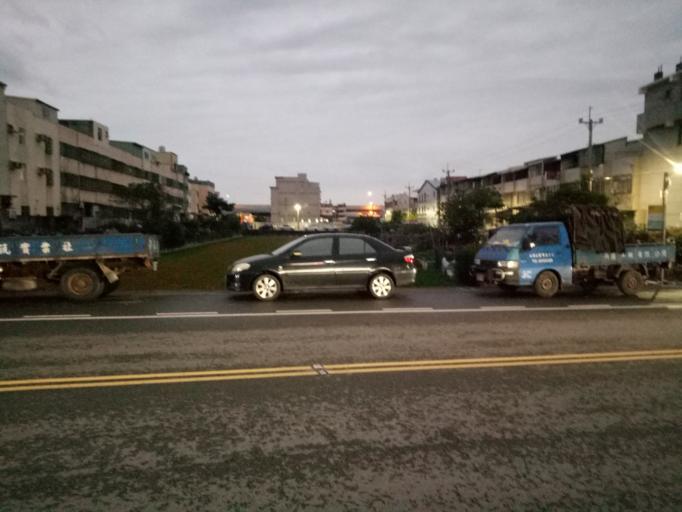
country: TW
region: Taiwan
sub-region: Changhua
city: Chang-hua
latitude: 24.2429
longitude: 120.5371
